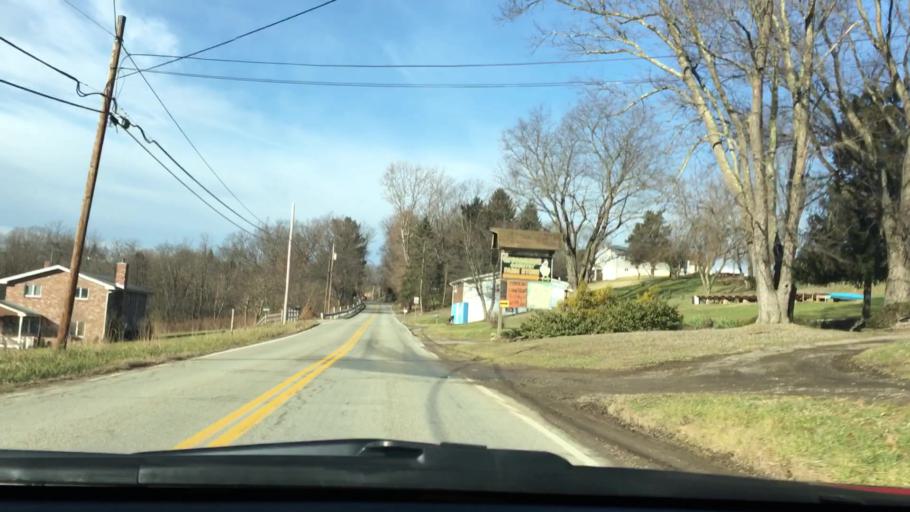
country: US
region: Pennsylvania
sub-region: Westmoreland County
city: Collinsburg
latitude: 40.2372
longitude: -79.7014
